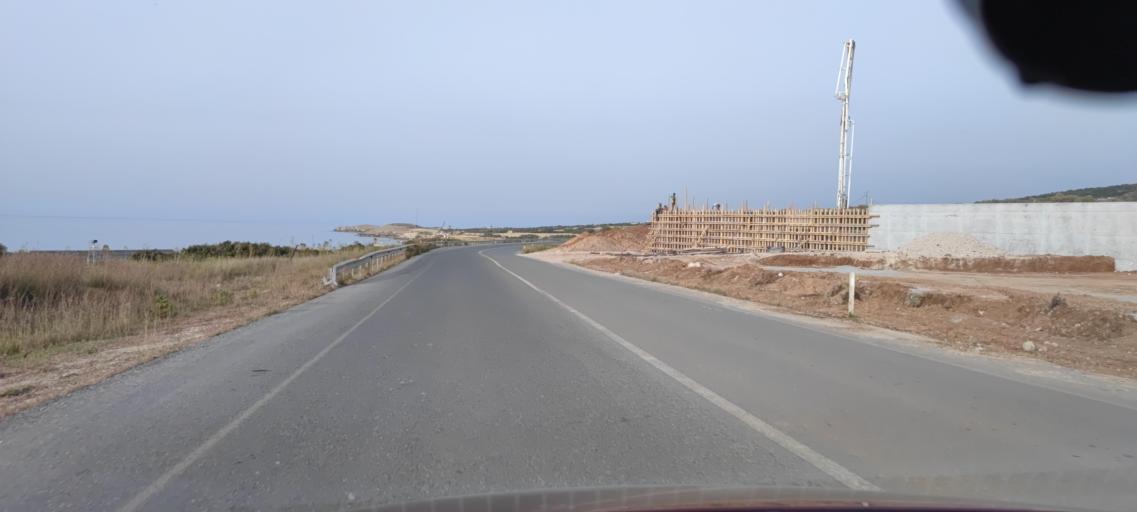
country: CY
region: Ammochostos
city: Leonarisso
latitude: 35.5573
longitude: 34.2336
